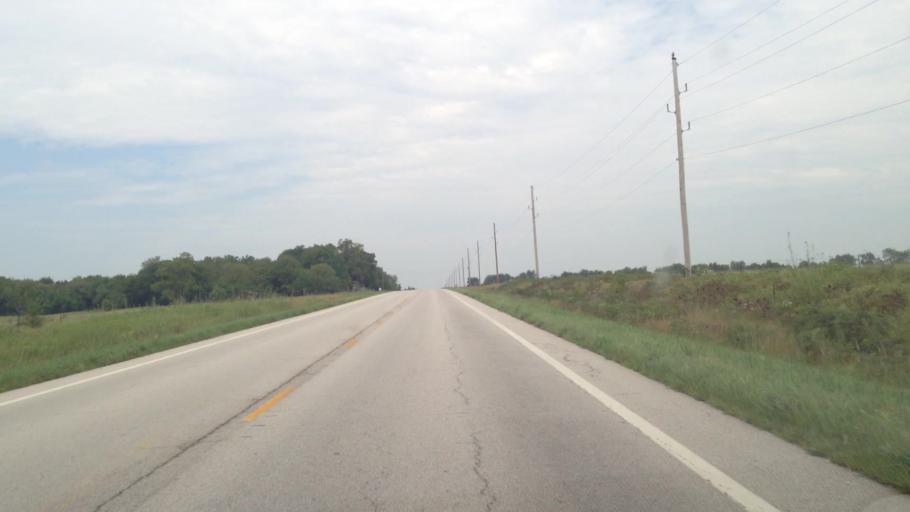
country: US
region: Kansas
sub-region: Allen County
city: Iola
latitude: 37.9661
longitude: -95.1701
